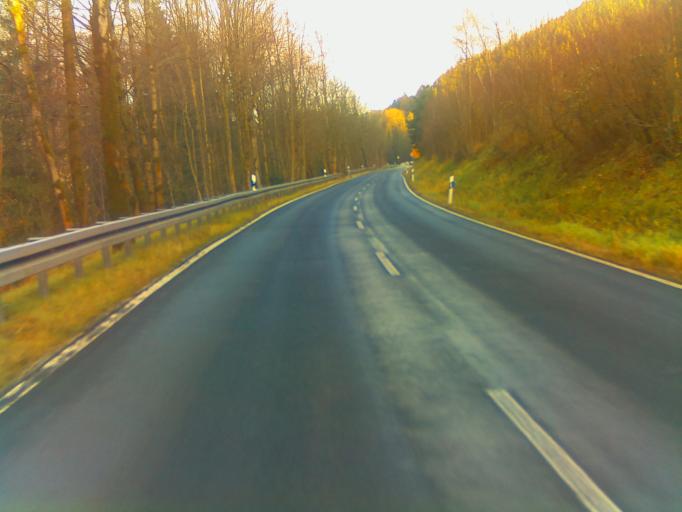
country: DE
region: Thuringia
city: Katzhutte
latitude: 50.5699
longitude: 11.0711
